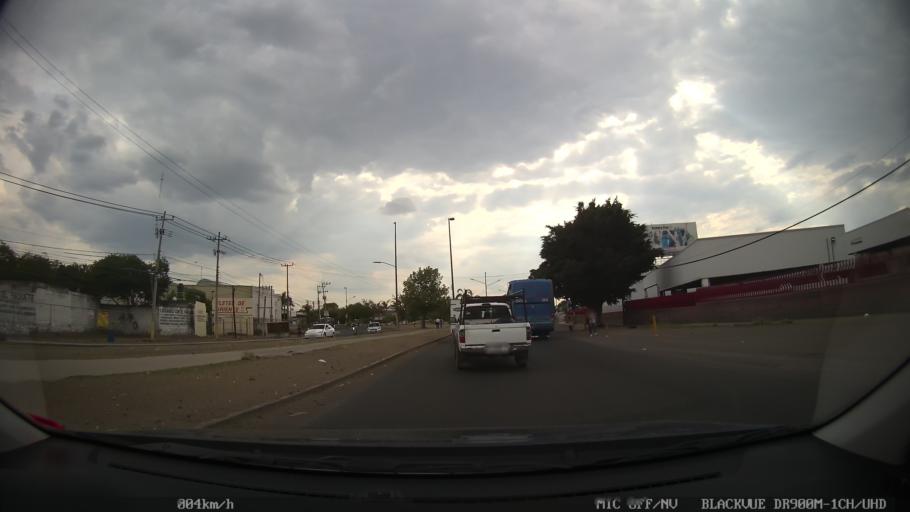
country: MX
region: Jalisco
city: Tlaquepaque
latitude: 20.6165
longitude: -103.2829
